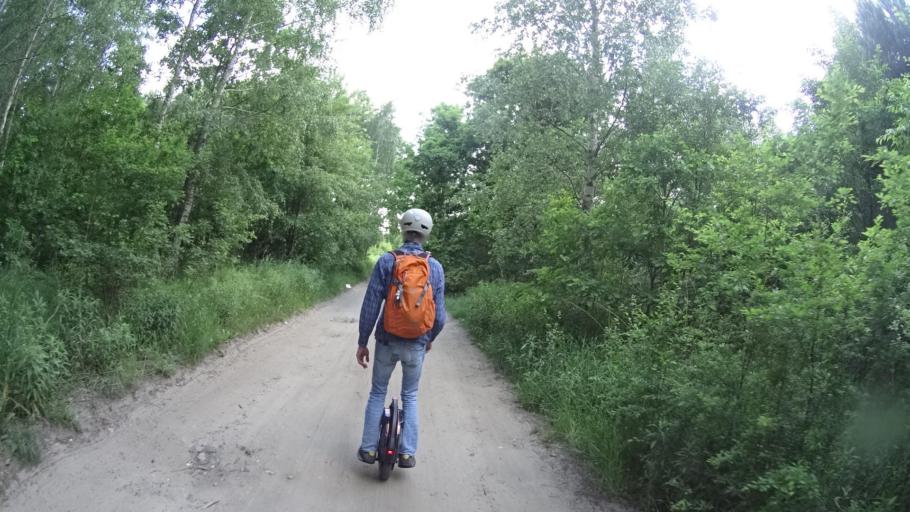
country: PL
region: Masovian Voivodeship
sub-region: Powiat piaseczynski
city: Konstancin-Jeziorna
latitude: 52.0976
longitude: 21.1041
